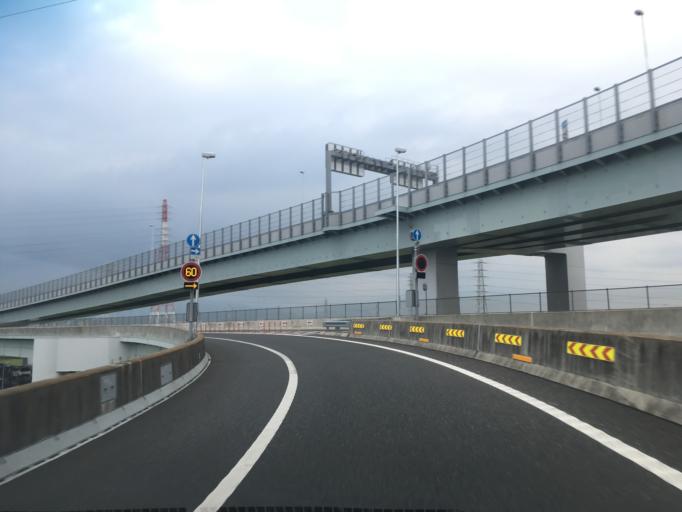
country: JP
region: Kanagawa
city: Chigasaki
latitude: 35.3504
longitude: 139.3921
